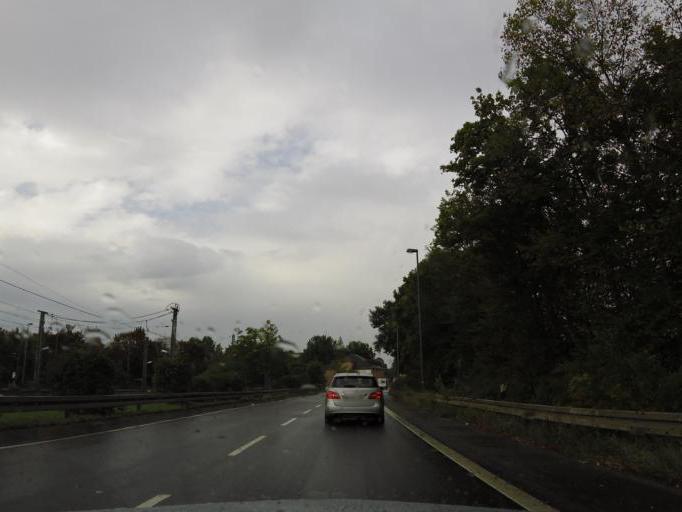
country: DE
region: Hesse
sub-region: Regierungsbezirk Darmstadt
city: Frankfurt am Main
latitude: 50.1500
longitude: 8.6382
